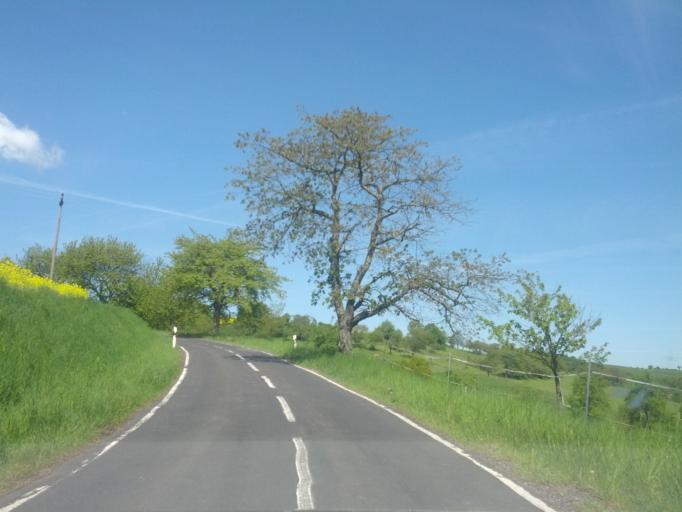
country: DE
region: Thuringia
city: Treffurt
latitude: 51.1065
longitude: 10.2168
